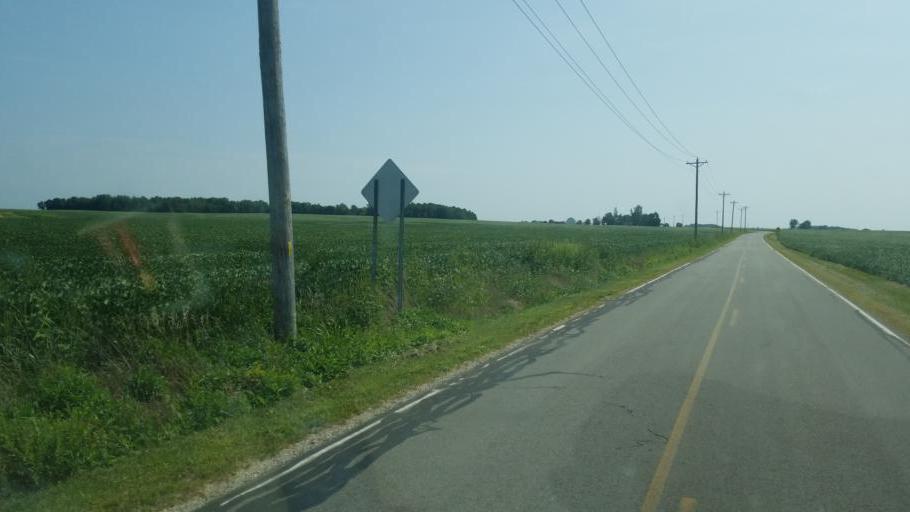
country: US
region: Ohio
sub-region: Richland County
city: Shelby
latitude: 40.8814
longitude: -82.7430
